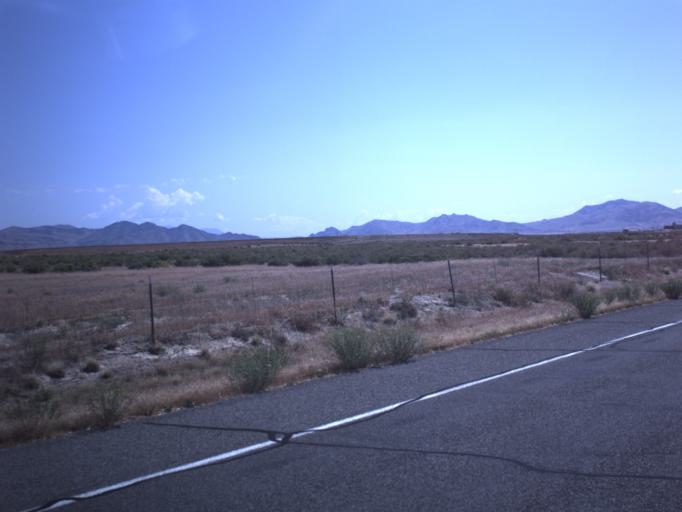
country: US
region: Utah
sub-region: Millard County
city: Delta
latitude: 39.4685
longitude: -112.4524
